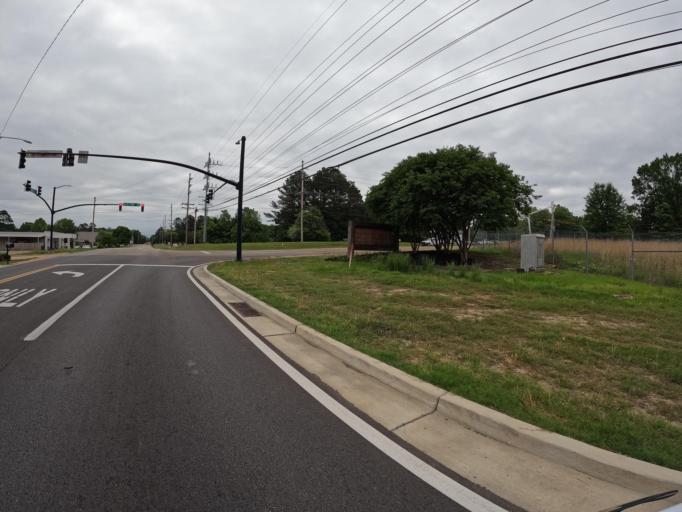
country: US
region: Mississippi
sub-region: Lee County
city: Tupelo
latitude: 34.2647
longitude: -88.7578
